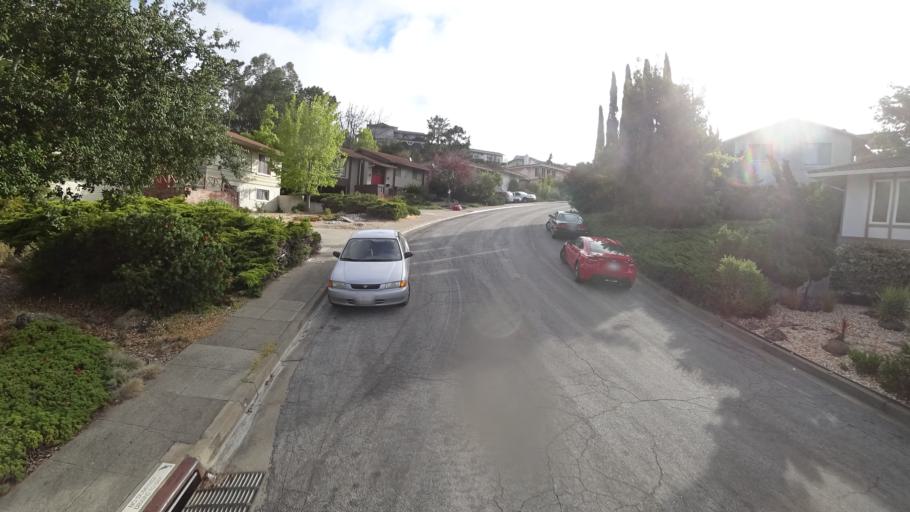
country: US
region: California
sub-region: Alameda County
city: Fairview
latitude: 37.6529
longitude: -122.0392
